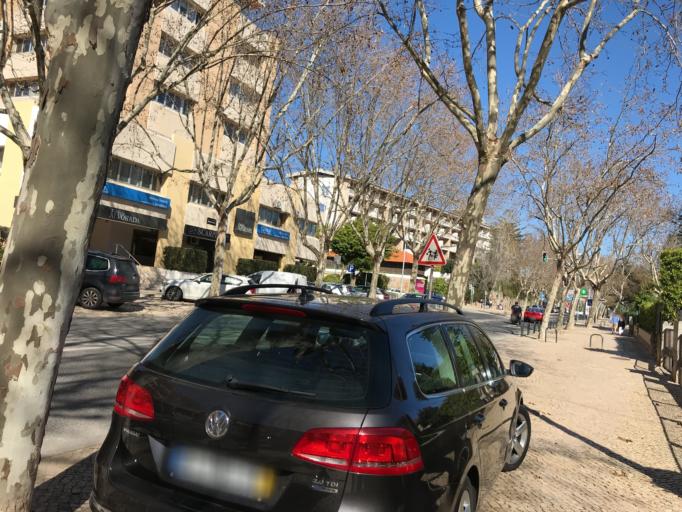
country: PT
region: Lisbon
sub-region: Cascais
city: Cascais
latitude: 38.6993
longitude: -9.4271
